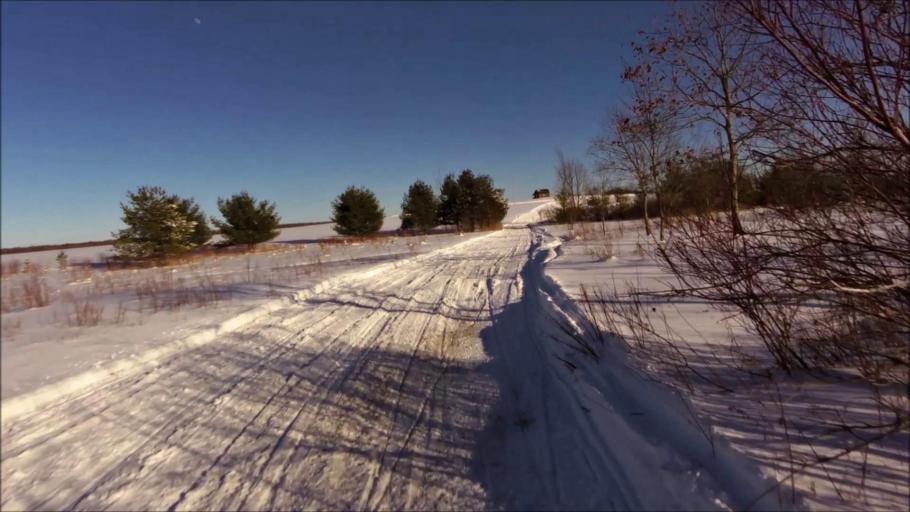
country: US
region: New York
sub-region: Chautauqua County
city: Mayville
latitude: 42.2849
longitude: -79.4299
